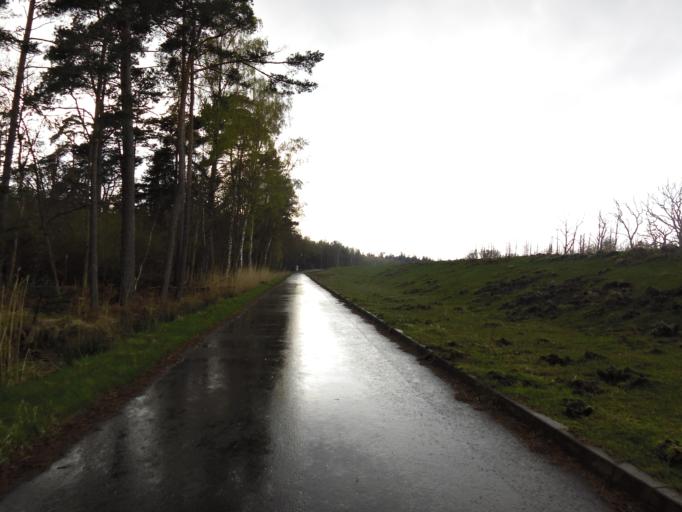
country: DE
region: Mecklenburg-Vorpommern
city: Barth
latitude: 54.4359
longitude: 12.7826
